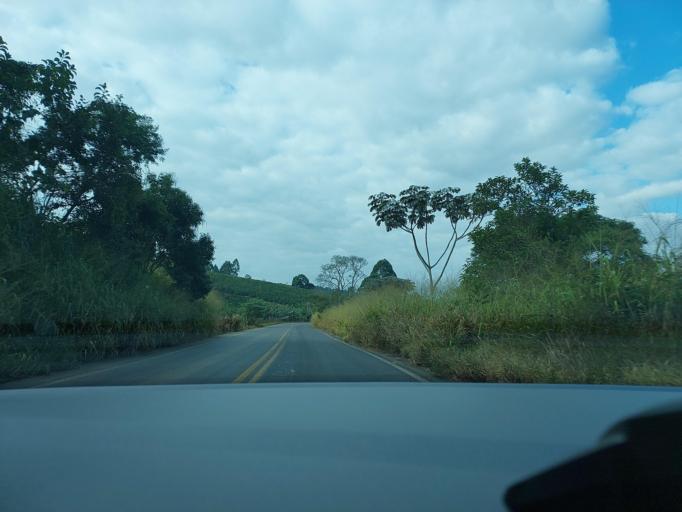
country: BR
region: Minas Gerais
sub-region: Vicosa
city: Vicosa
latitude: -20.8406
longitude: -42.7046
